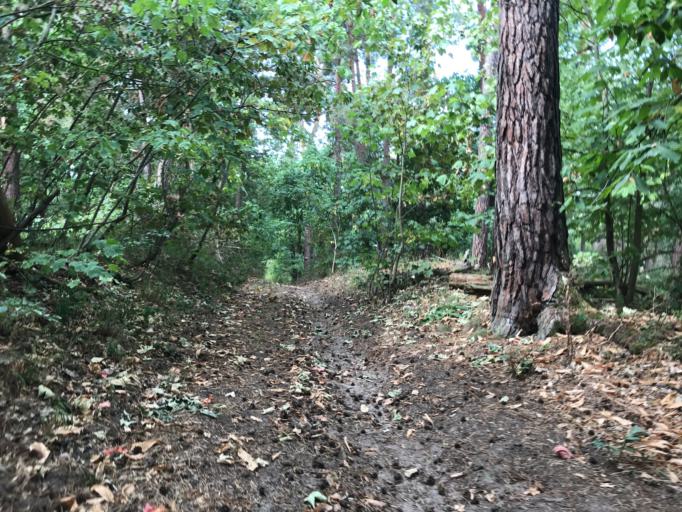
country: DE
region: Rheinland-Pfalz
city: Budenheim
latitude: 50.0097
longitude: 8.1591
